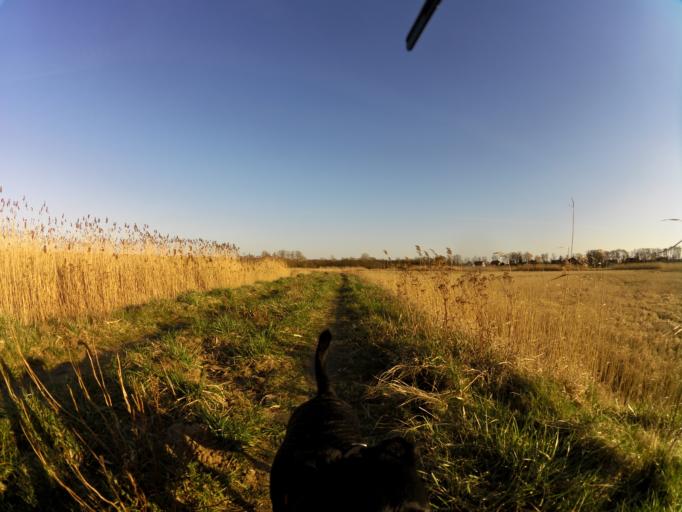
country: PL
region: West Pomeranian Voivodeship
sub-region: Powiat policki
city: Nowe Warpno
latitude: 53.7264
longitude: 14.2973
